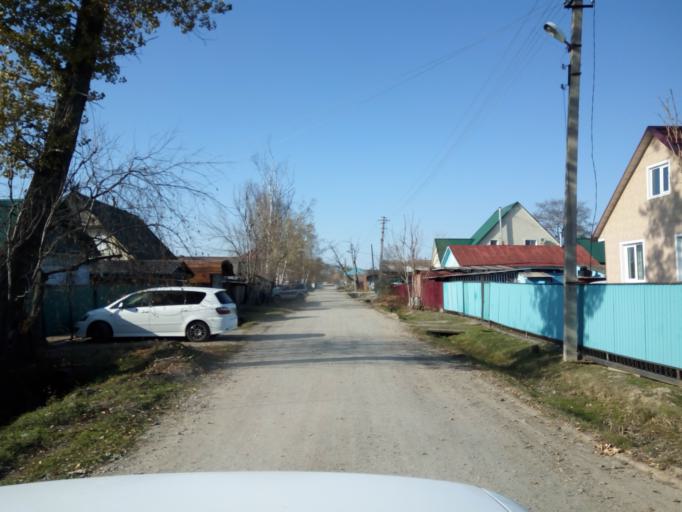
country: RU
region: Primorskiy
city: Dal'nerechensk
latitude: 45.9234
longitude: 133.7333
